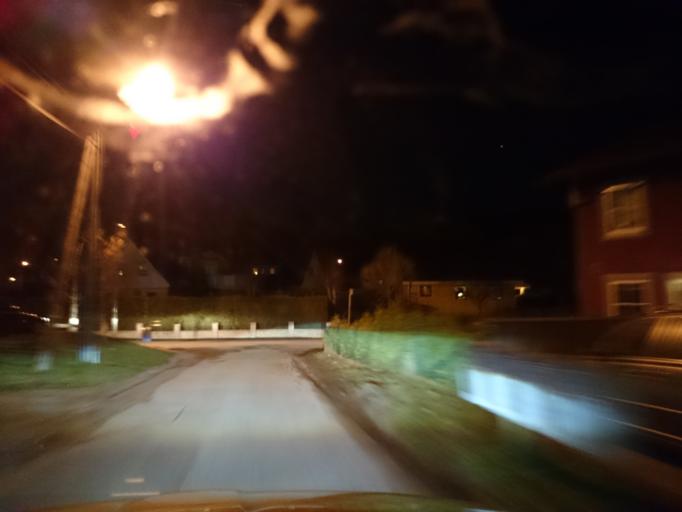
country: SE
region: Stockholm
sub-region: Huddinge Kommun
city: Segeltorp
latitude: 59.2721
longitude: 17.9287
